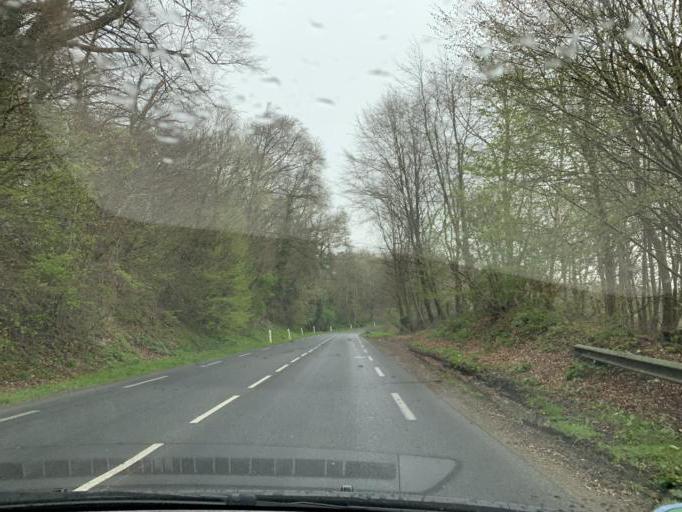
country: FR
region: Haute-Normandie
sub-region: Departement de la Seine-Maritime
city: Cany-Barville
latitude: 49.7871
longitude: 0.6472
